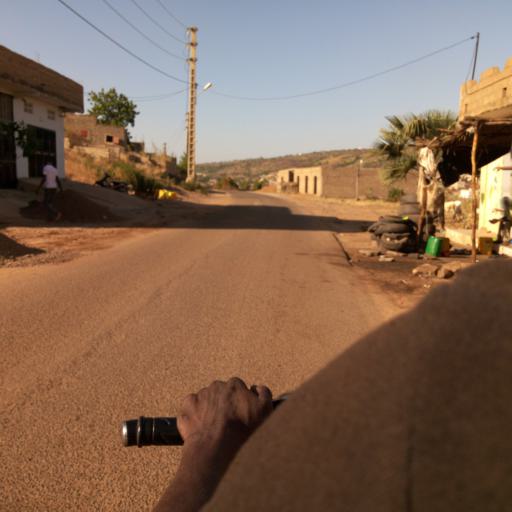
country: ML
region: Bamako
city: Bamako
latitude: 12.6599
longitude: -8.0384
